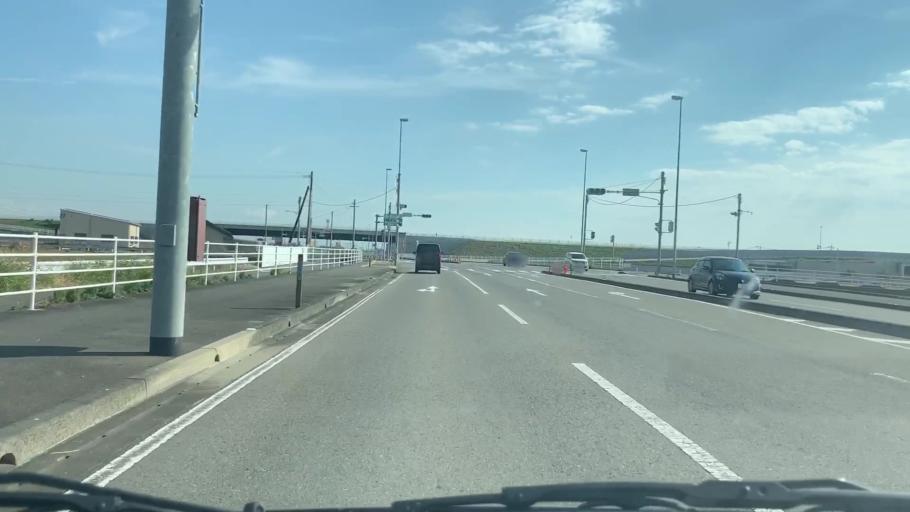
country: JP
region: Saga Prefecture
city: Saga-shi
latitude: 33.2207
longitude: 130.2120
